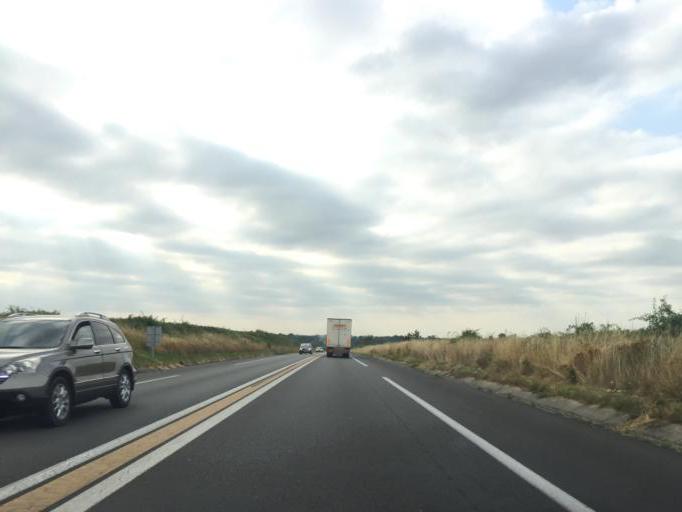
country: FR
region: Auvergne
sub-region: Departement de l'Allier
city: Diou
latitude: 46.4950
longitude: 3.7997
